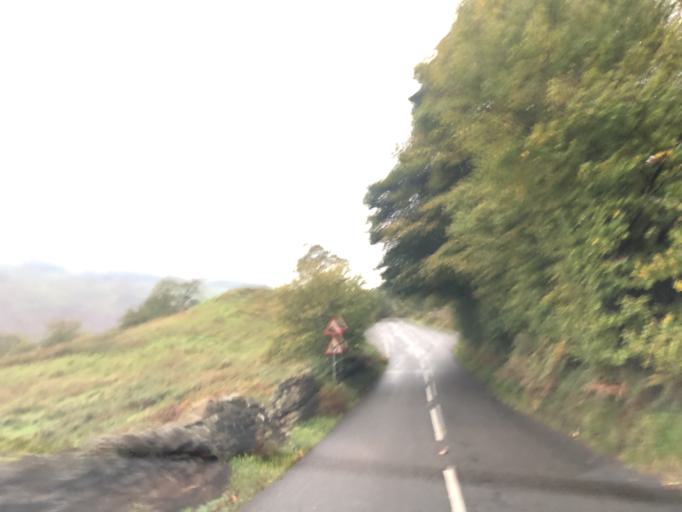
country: GB
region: England
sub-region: Cumbria
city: Windermere
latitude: 54.4352
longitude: -2.9020
